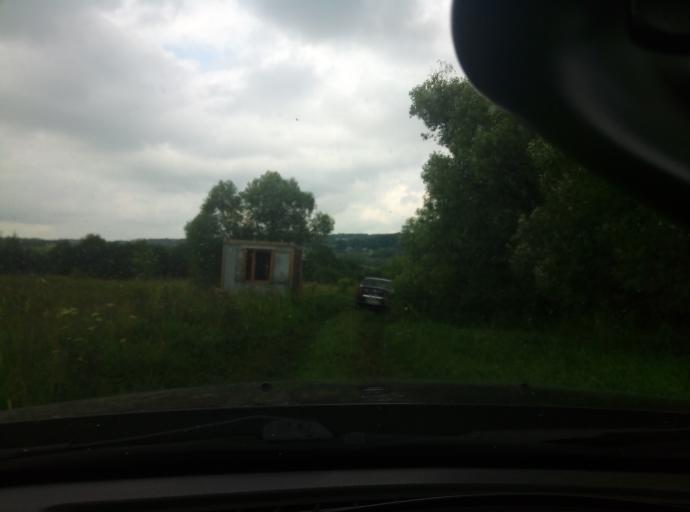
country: RU
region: Tula
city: Shvartsevskiy
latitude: 54.0838
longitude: 38.0212
